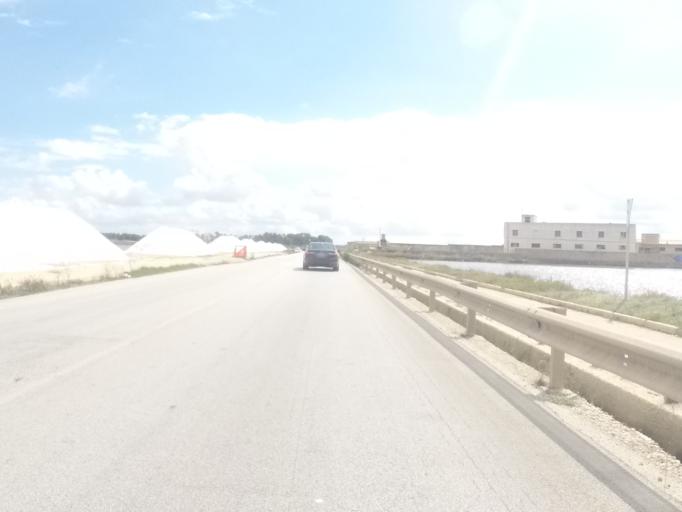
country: IT
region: Sicily
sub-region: Trapani
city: Trapani
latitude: 37.9953
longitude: 12.5348
